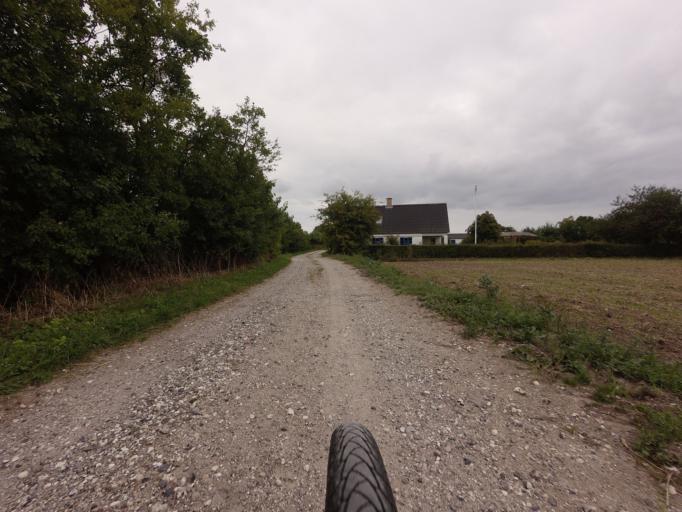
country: DK
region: Zealand
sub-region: Stevns Kommune
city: Store Heddinge
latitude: 55.3297
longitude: 12.4496
